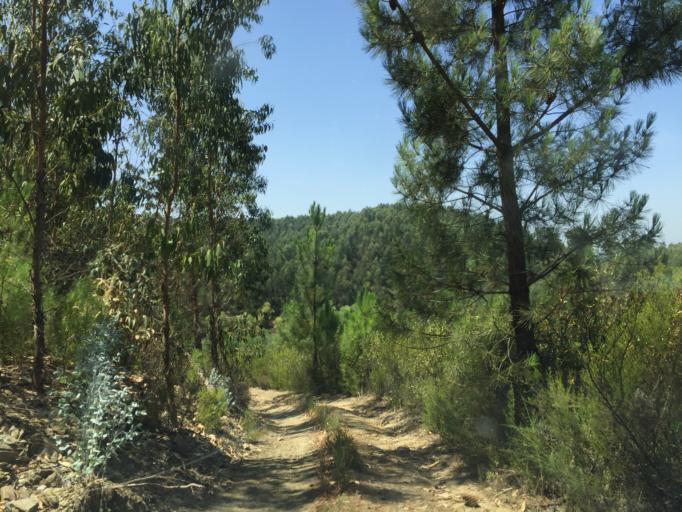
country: PT
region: Santarem
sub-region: Ferreira do Zezere
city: Ferreira do Zezere
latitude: 39.6512
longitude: -8.3173
